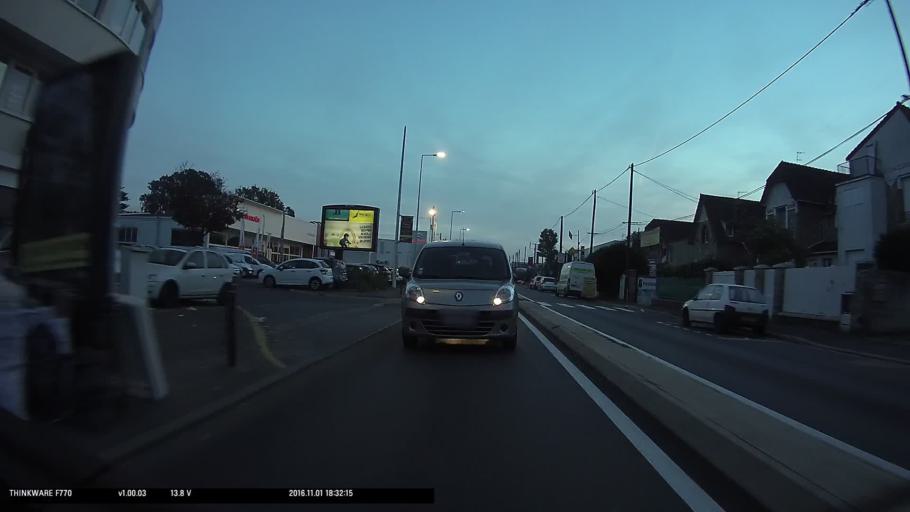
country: FR
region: Ile-de-France
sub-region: Departement de l'Essonne
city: Villemoisson-sur-Orge
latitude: 48.6532
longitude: 2.3378
